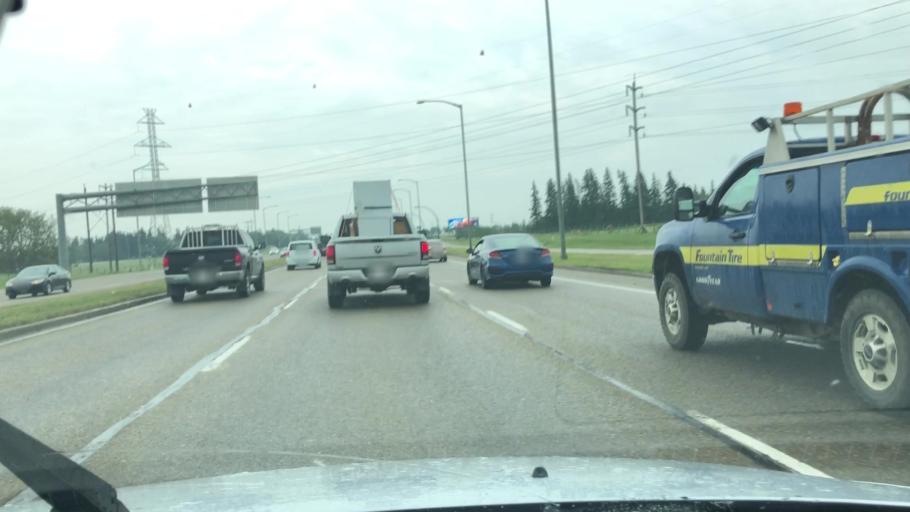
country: CA
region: Alberta
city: St. Albert
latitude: 53.6148
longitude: -113.5968
